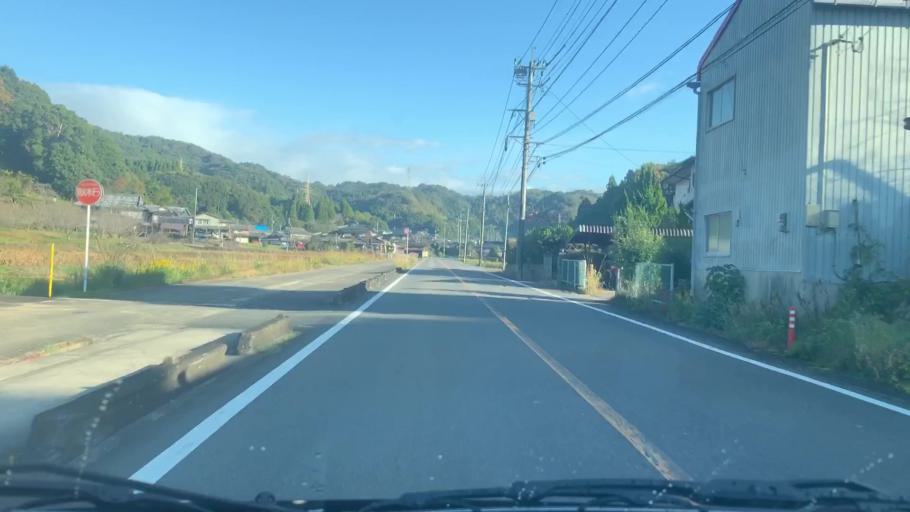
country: JP
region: Saga Prefecture
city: Takeocho-takeo
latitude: 33.2296
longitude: 130.0598
